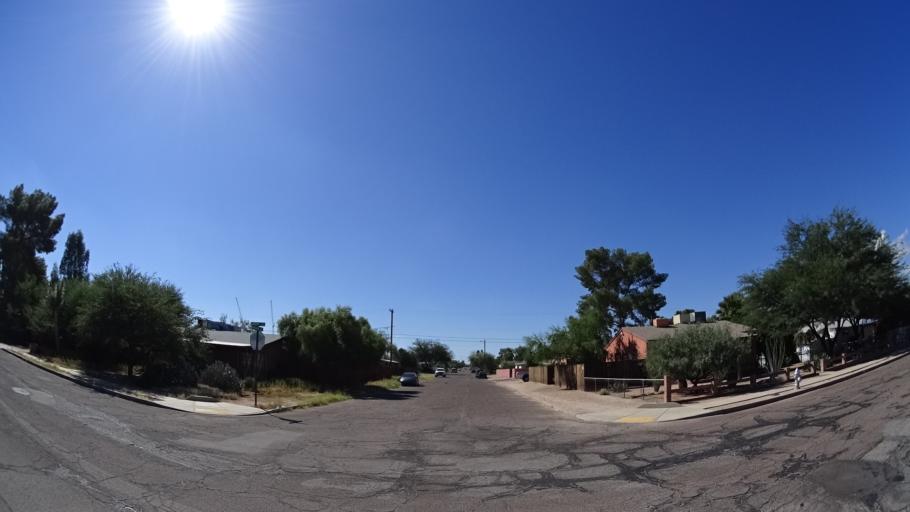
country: US
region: Arizona
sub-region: Pima County
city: Tucson
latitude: 32.2479
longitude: -110.9513
